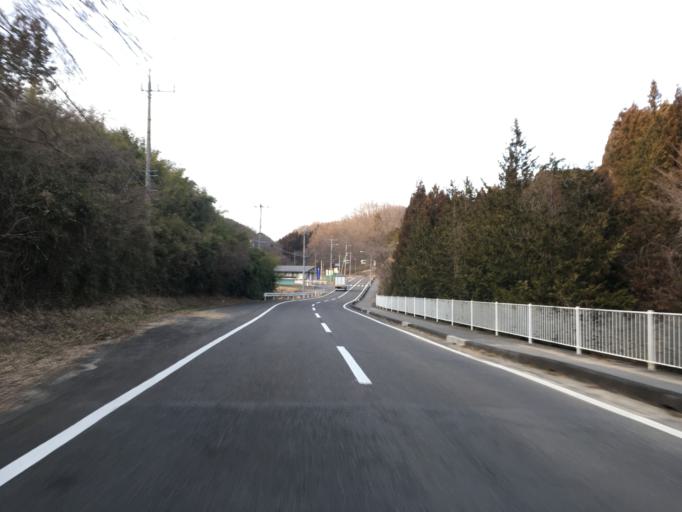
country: JP
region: Ibaraki
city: Daigo
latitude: 36.7766
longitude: 140.4269
